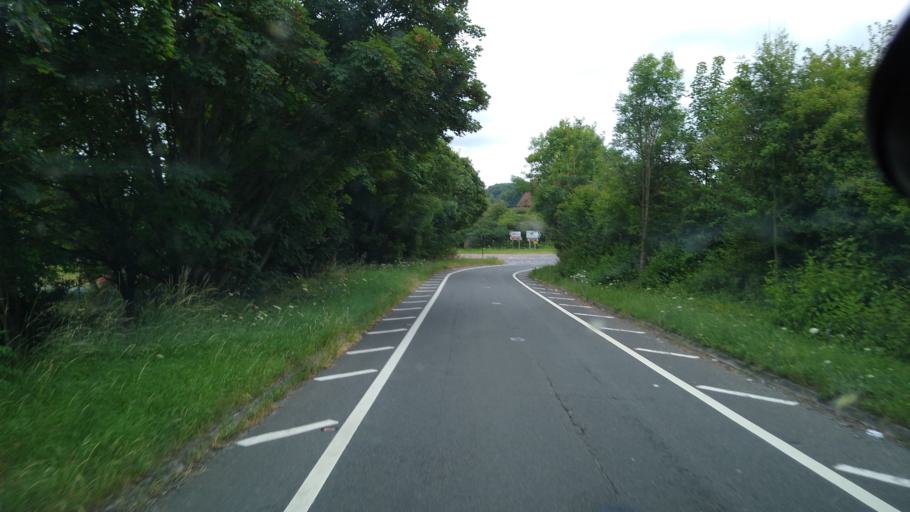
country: GB
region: England
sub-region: Hampshire
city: Alton
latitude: 51.1364
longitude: -0.9760
